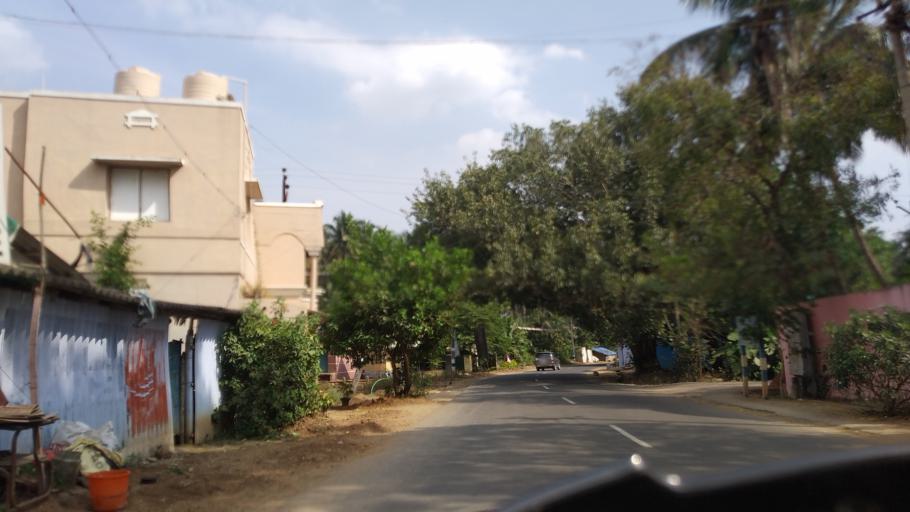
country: IN
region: Tamil Nadu
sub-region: Coimbatore
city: Perur
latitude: 10.9559
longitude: 76.7601
